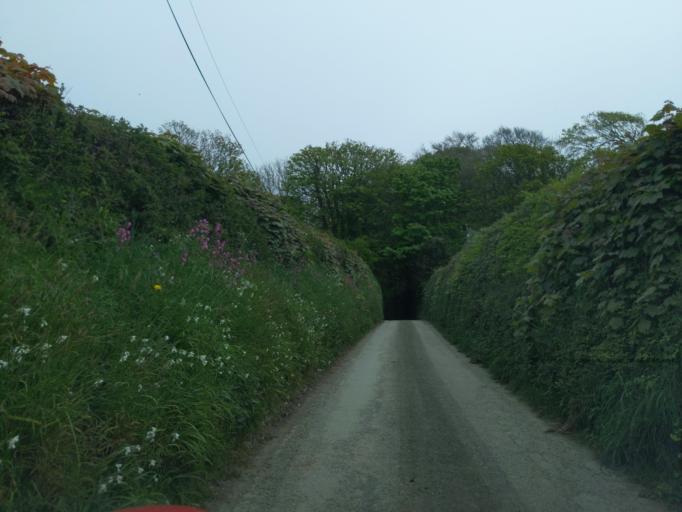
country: GB
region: England
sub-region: Cornwall
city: St Austell
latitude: 50.3087
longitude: -4.7649
